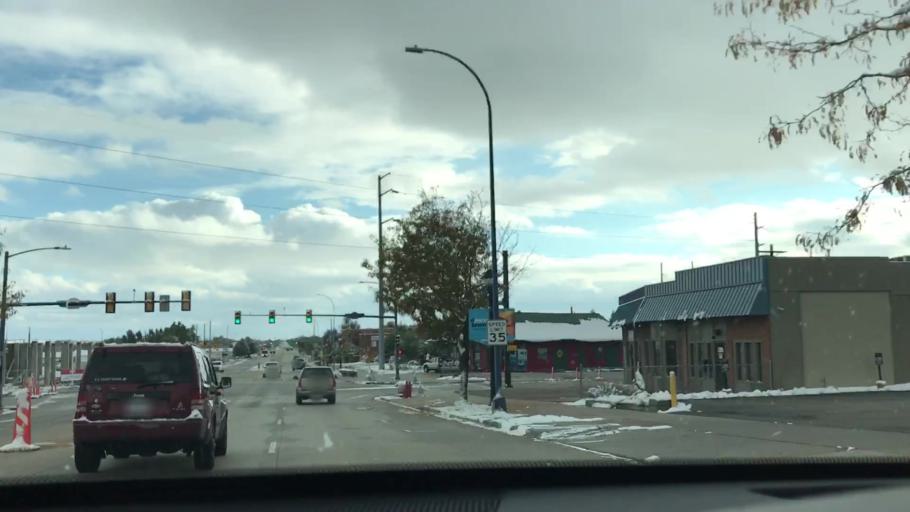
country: US
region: Colorado
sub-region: Boulder County
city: Longmont
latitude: 40.1624
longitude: -105.1026
